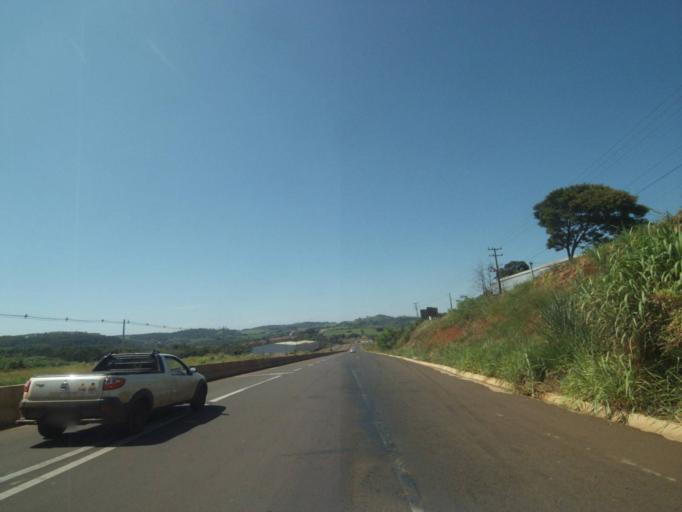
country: BR
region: Parana
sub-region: Londrina
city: Londrina
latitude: -23.3909
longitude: -51.1342
